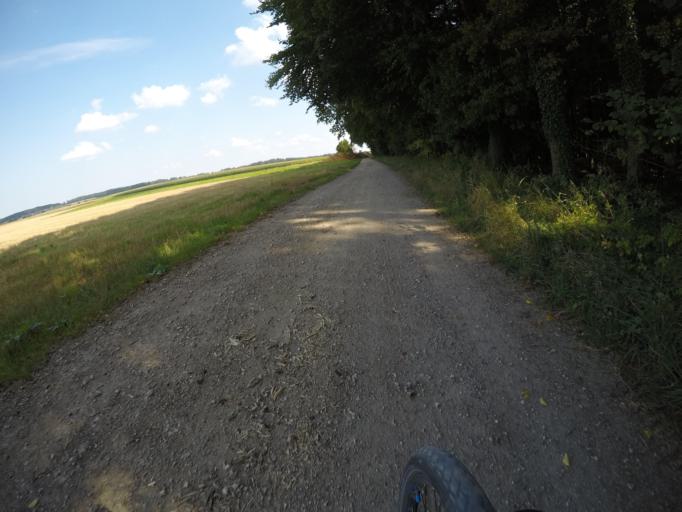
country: DE
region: Bavaria
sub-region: Swabia
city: Biberbach
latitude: 48.5417
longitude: 10.7892
